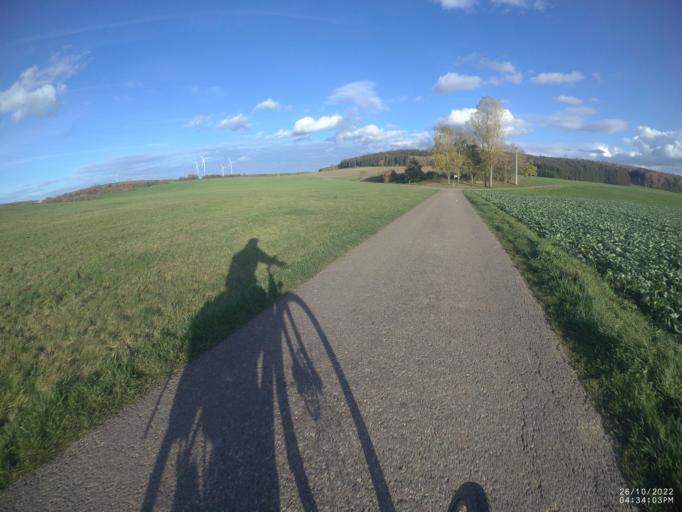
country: DE
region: Baden-Wuerttemberg
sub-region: Regierungsbezirk Stuttgart
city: Hohenstadt
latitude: 48.5262
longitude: 9.6774
